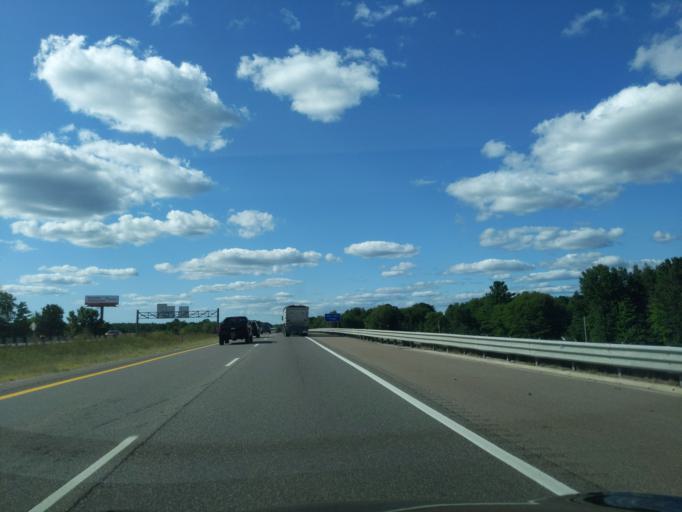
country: US
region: Michigan
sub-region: Muskegon County
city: Fruitport
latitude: 43.0778
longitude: -86.0851
